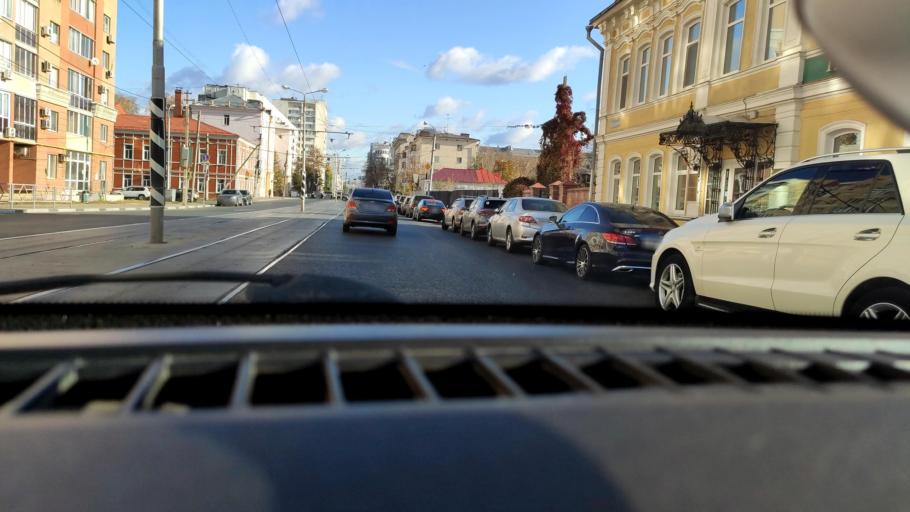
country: RU
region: Samara
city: Samara
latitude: 53.1995
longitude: 50.1076
